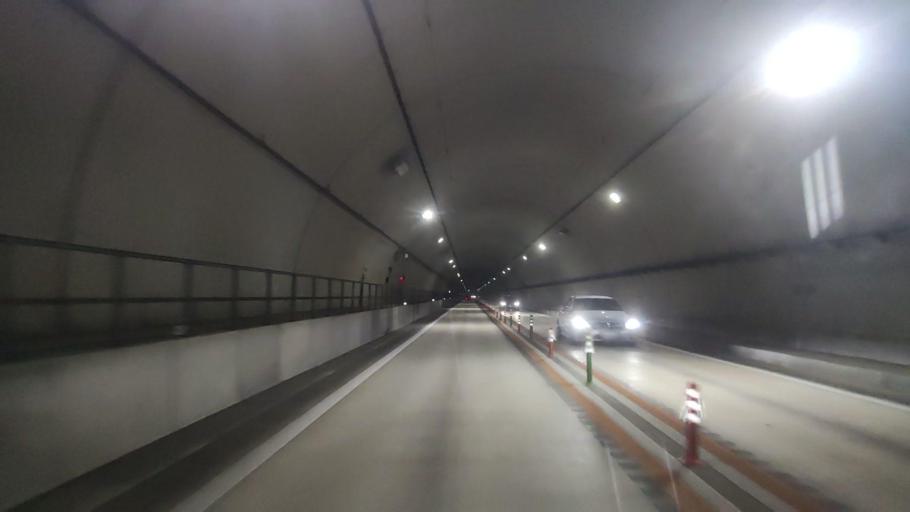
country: JP
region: Wakayama
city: Tanabe
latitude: 33.5669
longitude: 135.4919
